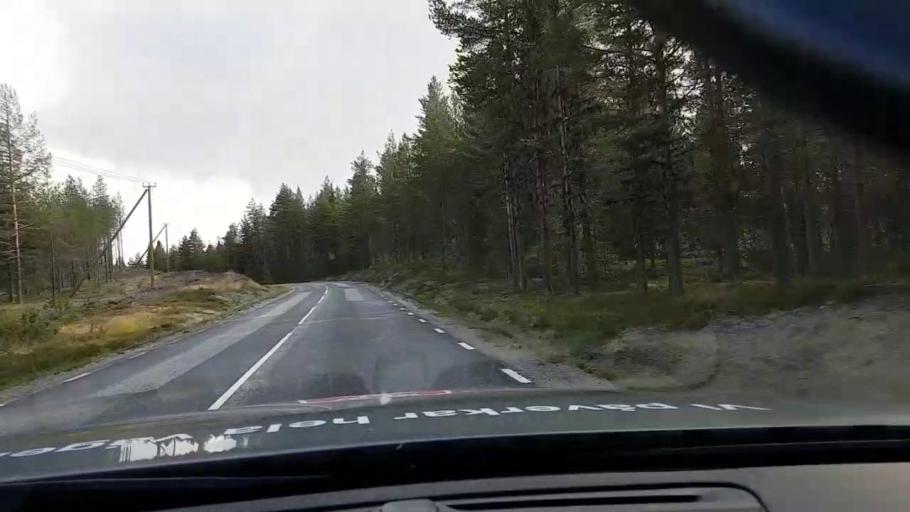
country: SE
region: Vaesterbotten
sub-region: Asele Kommun
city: Asele
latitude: 63.8516
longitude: 17.3942
